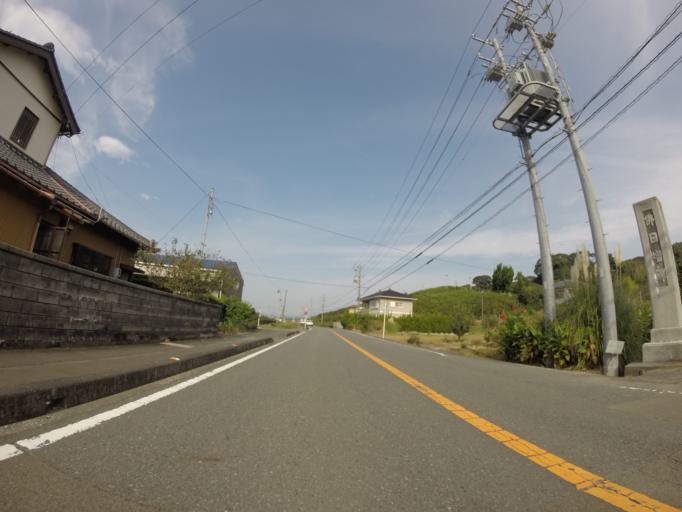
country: JP
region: Shizuoka
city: Sagara
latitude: 34.7510
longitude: 138.2125
